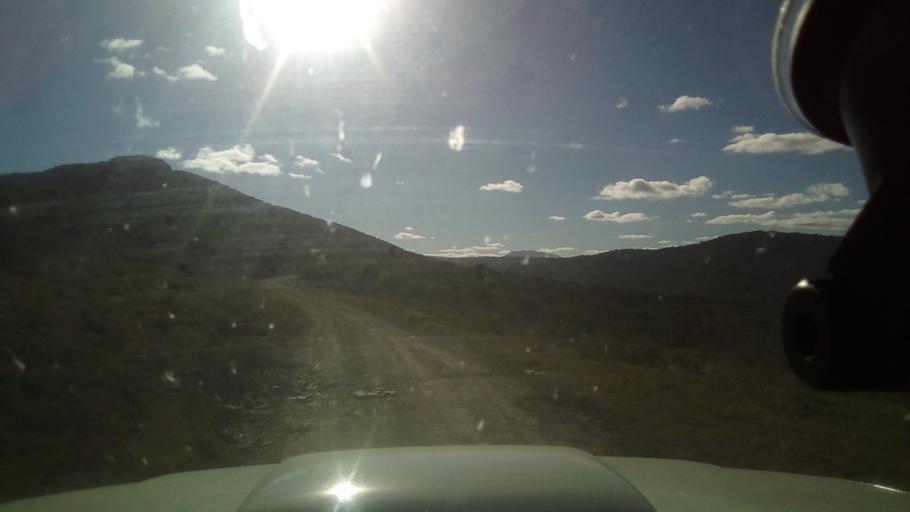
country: ZA
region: Eastern Cape
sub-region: Buffalo City Metropolitan Municipality
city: Bhisho
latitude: -32.7433
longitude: 27.3510
